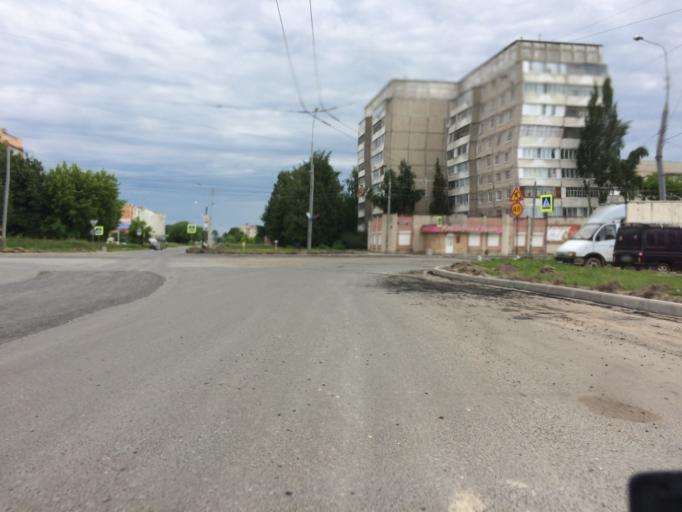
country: RU
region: Mariy-El
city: Yoshkar-Ola
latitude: 56.6444
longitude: 47.8575
